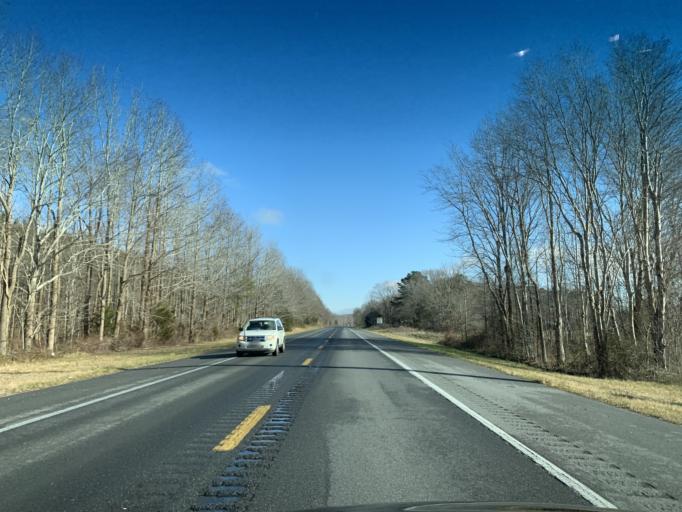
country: US
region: Maryland
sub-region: Worcester County
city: Berlin
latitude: 38.3741
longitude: -75.2508
